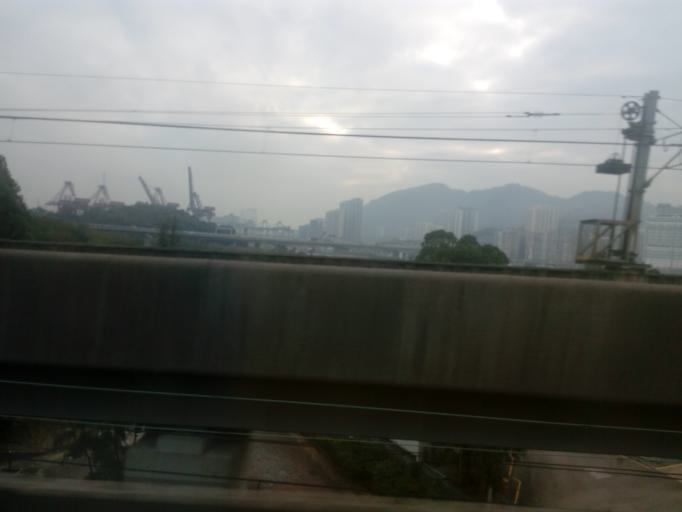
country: HK
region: Tsuen Wan
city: Tsuen Wan
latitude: 22.3546
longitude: 114.1181
